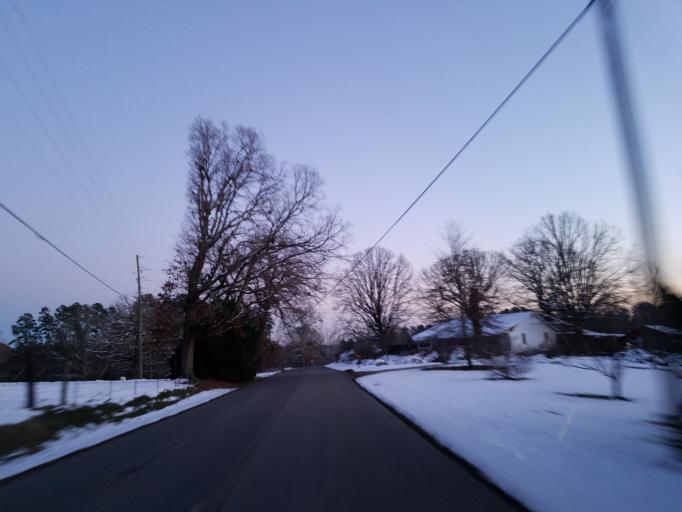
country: US
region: Georgia
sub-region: Pickens County
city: Nelson
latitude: 34.3616
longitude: -84.3696
